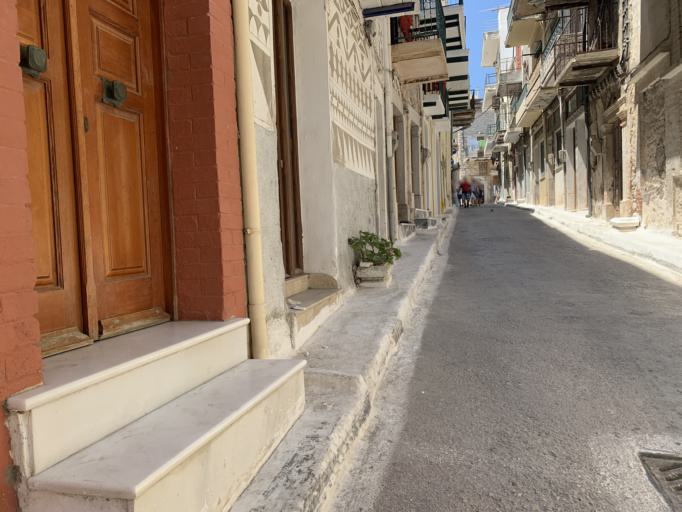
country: GR
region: North Aegean
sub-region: Chios
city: Thymiana
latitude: 38.2270
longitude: 25.9999
